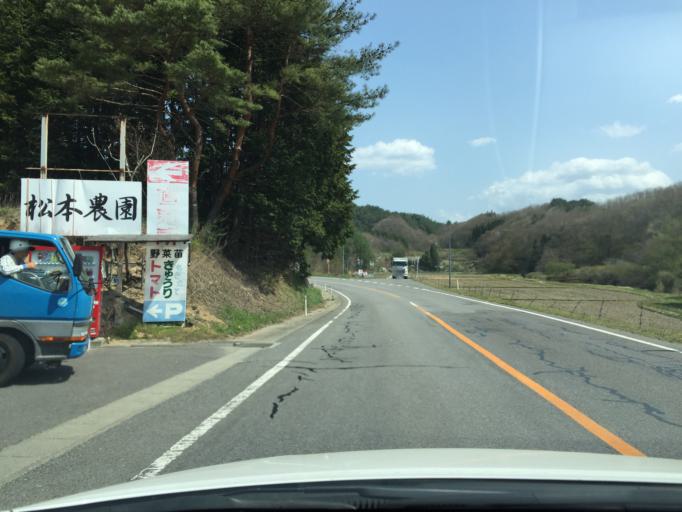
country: JP
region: Fukushima
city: Funehikimachi-funehiki
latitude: 37.4464
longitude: 140.7754
